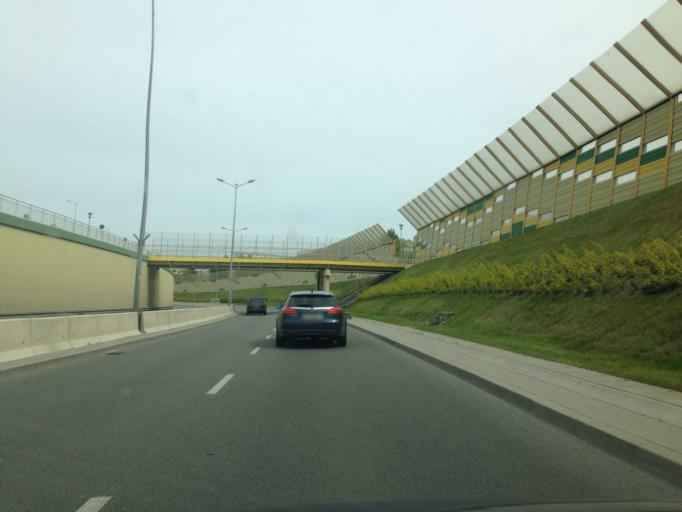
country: PL
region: Pomeranian Voivodeship
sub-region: Sopot
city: Sopot
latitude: 54.4237
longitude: 18.5694
